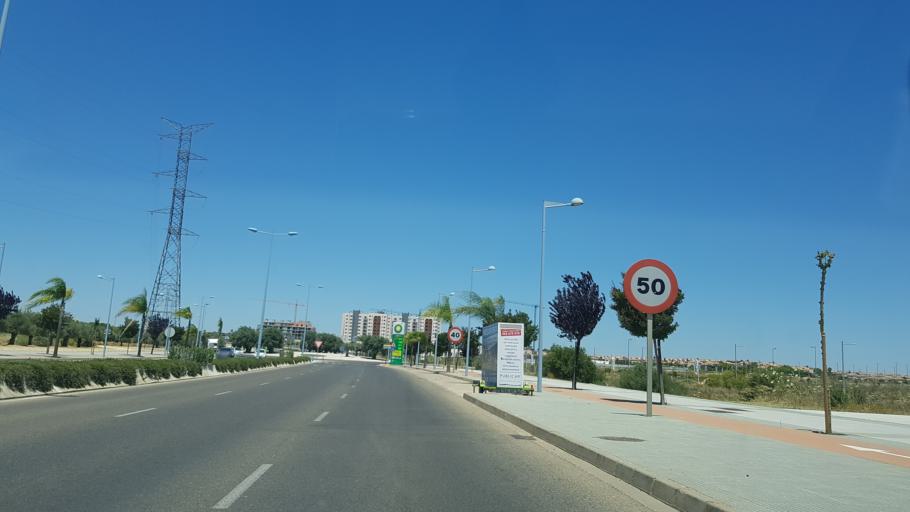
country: ES
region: Andalusia
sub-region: Provincia de Sevilla
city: Dos Hermanas
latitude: 37.3137
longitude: -5.9411
